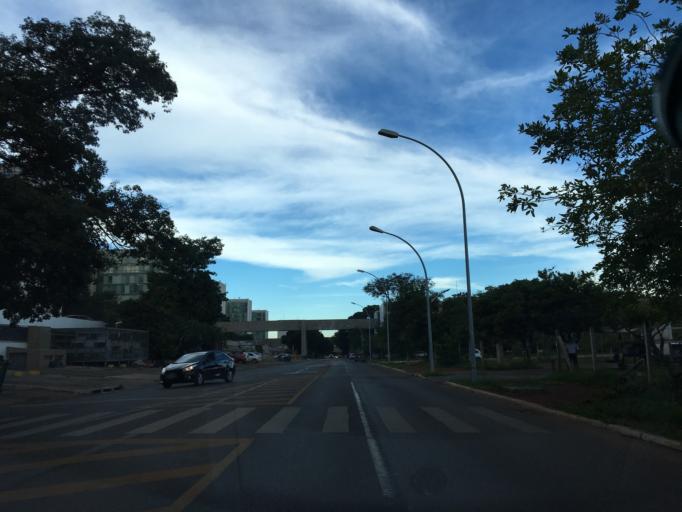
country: BR
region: Federal District
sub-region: Brasilia
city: Brasilia
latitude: -15.7999
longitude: -47.8732
